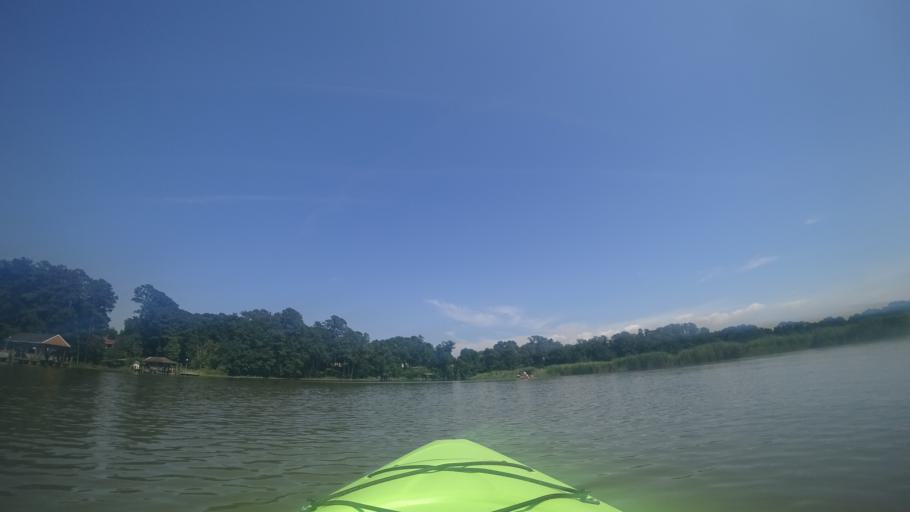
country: US
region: Virginia
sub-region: Isle of Wight County
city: Smithfield
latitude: 36.9692
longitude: -76.6140
